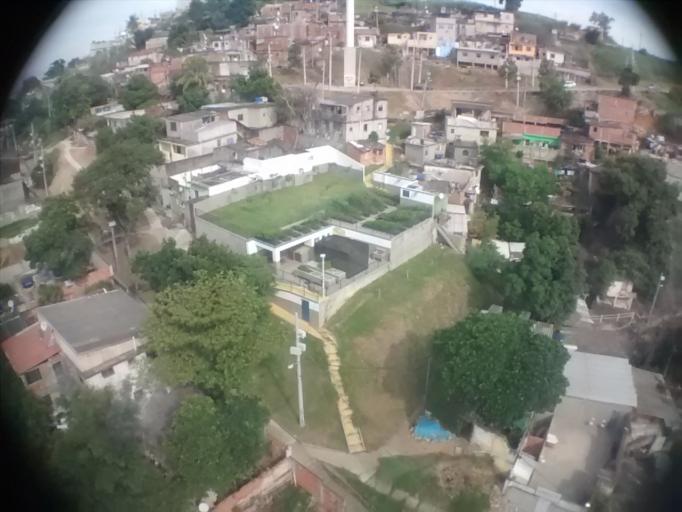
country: BR
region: Rio de Janeiro
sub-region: Rio De Janeiro
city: Rio de Janeiro
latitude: -22.8635
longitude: -43.2624
